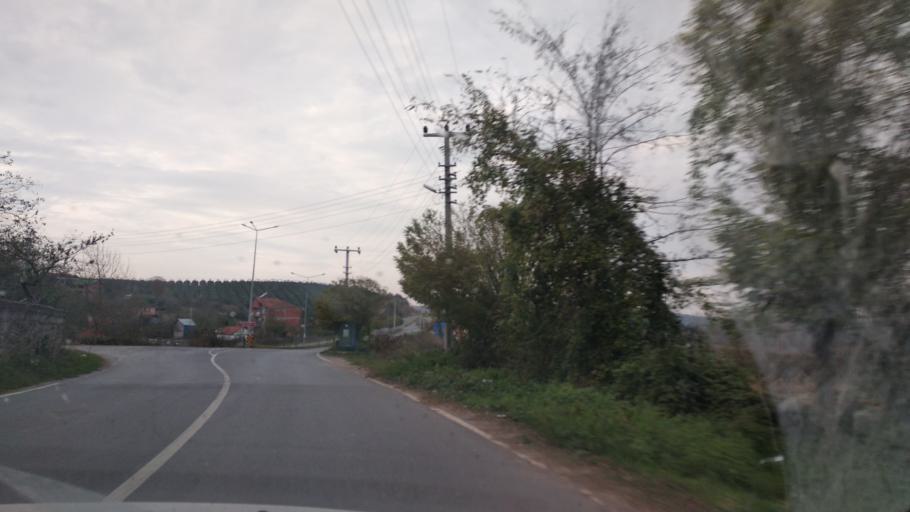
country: TR
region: Sakarya
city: Ortakoy
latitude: 41.0414
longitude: 30.6413
